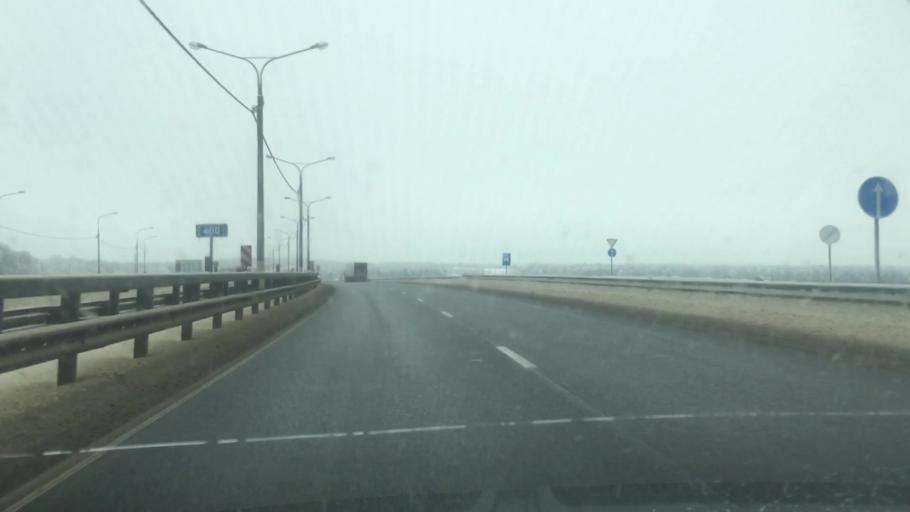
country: RU
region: Lipetsk
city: Yelets
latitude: 52.5428
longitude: 38.7223
